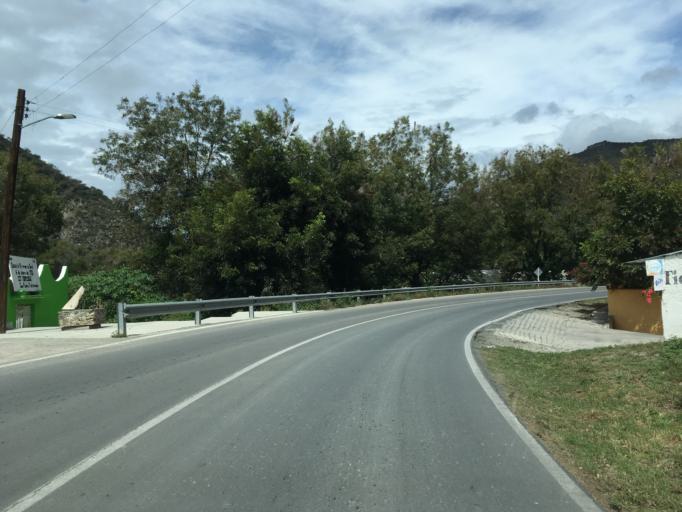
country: MX
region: Hidalgo
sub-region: San Agustin Metzquititlan
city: Mezquititlan
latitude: 20.4995
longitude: -98.7026
